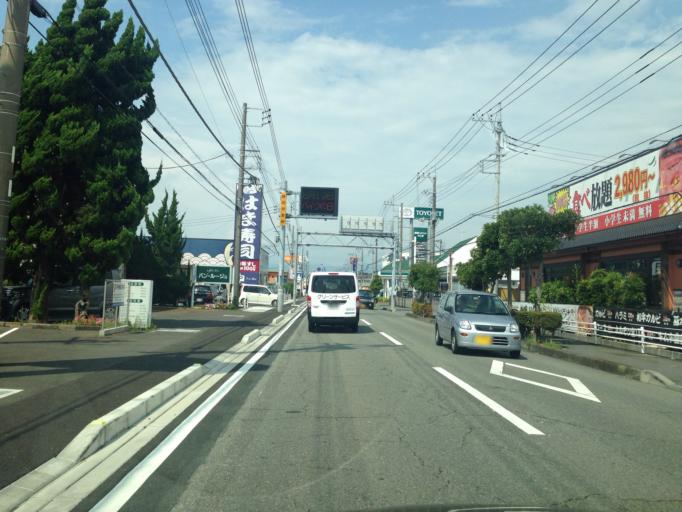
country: JP
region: Shizuoka
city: Mishima
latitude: 35.0043
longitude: 138.9408
